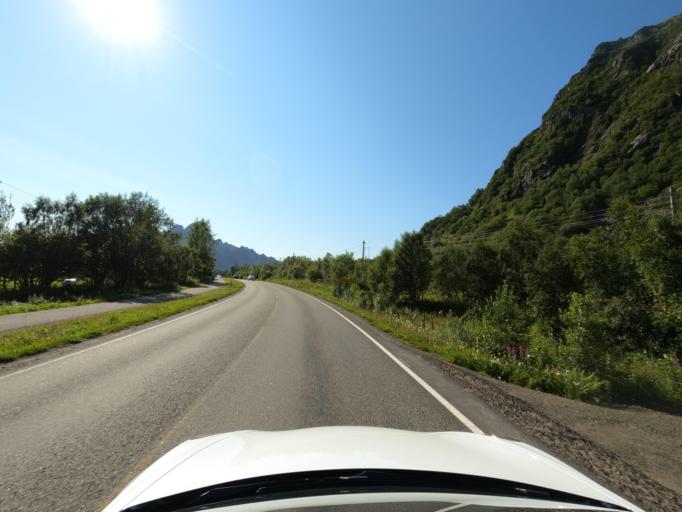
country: NO
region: Nordland
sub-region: Vagan
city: Kabelvag
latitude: 68.2149
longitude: 14.4013
